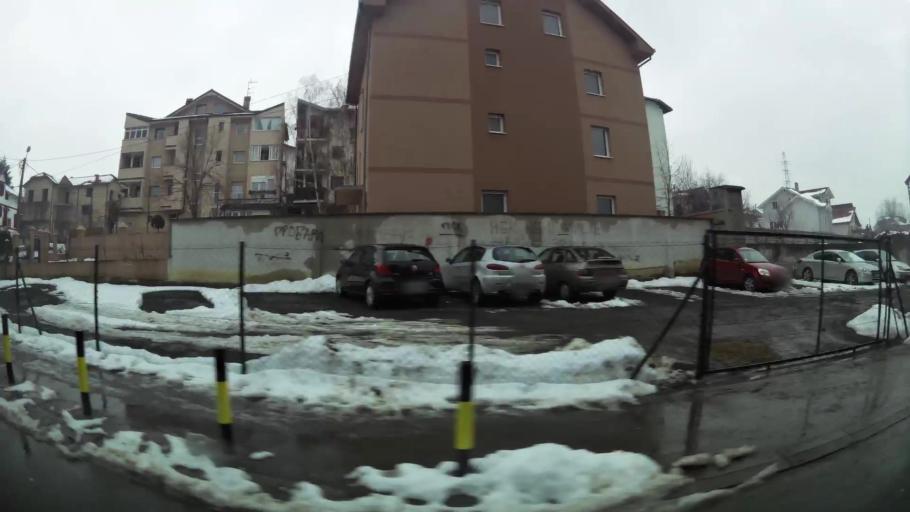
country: RS
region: Central Serbia
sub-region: Belgrade
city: Zvezdara
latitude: 44.7710
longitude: 20.5099
